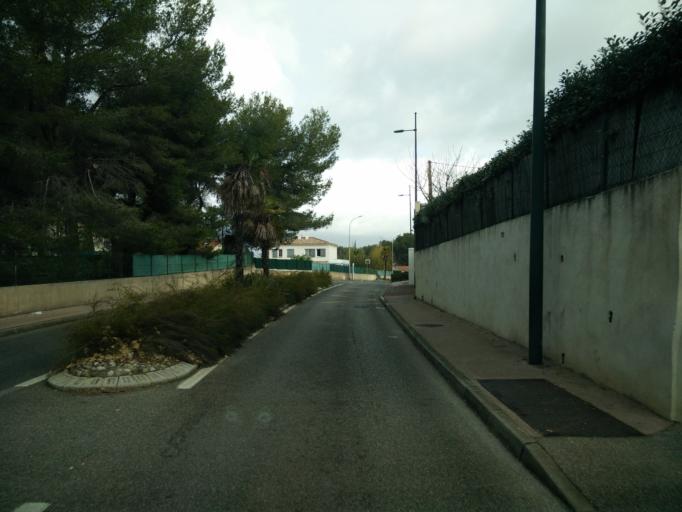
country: FR
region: Provence-Alpes-Cote d'Azur
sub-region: Departement du Var
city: Six-Fours-les-Plages
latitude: 43.0808
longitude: 5.8188
